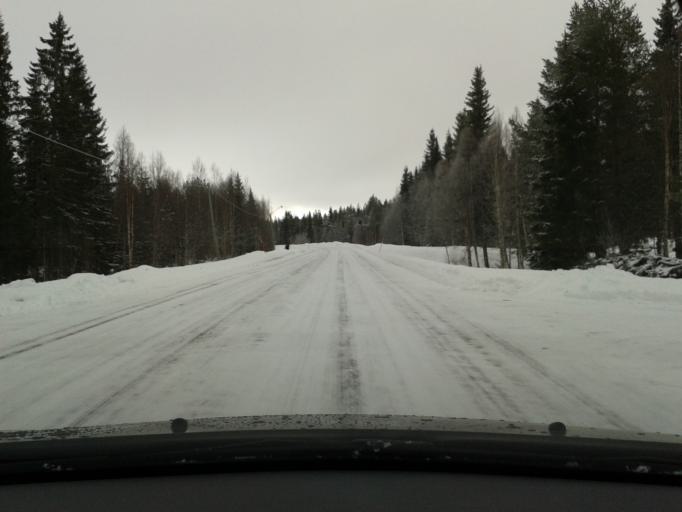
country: SE
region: Vaesterbotten
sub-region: Vilhelmina Kommun
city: Sjoberg
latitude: 64.8308
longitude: 15.9427
